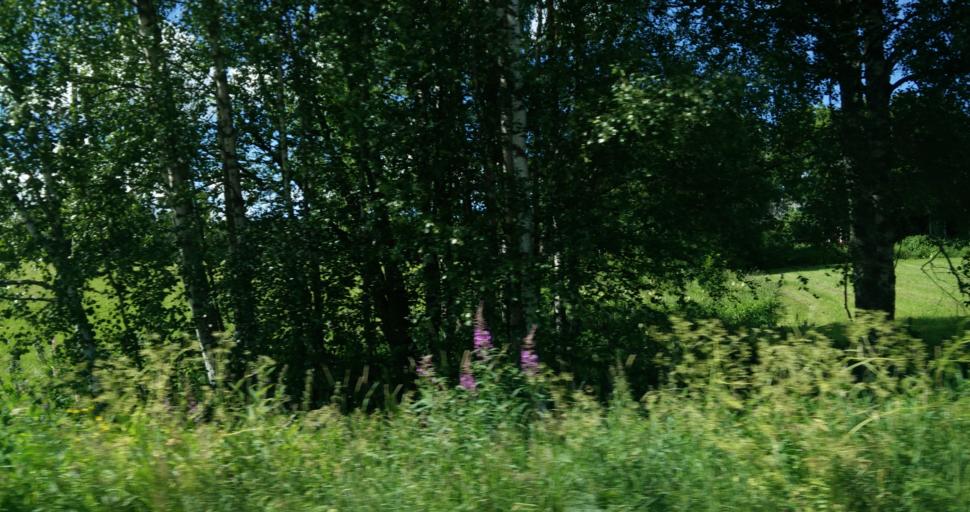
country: SE
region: Vaermland
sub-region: Hagfors Kommun
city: Hagfors
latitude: 60.0354
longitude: 13.6294
